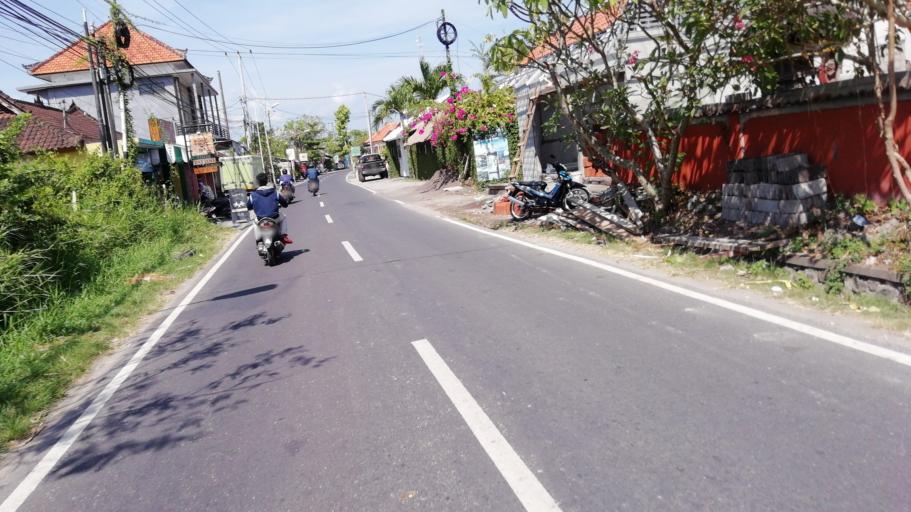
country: ID
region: Bali
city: Banjar Gunungpande
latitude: -8.6456
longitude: 115.1411
